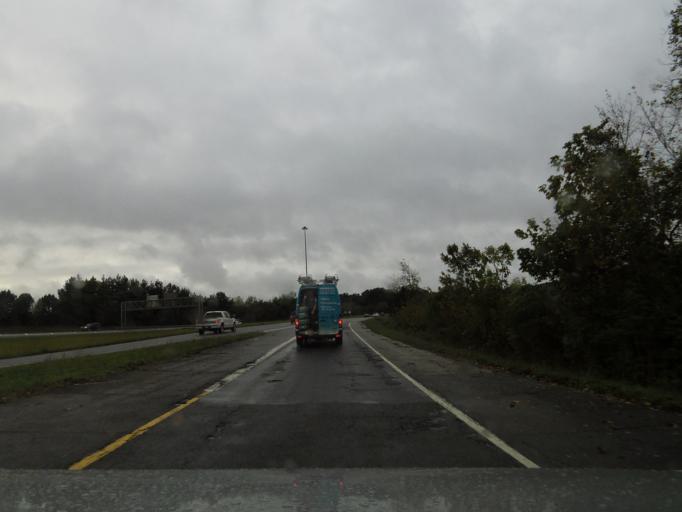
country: US
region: Tennessee
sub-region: Blount County
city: Alcoa
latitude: 35.7895
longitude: -83.9917
